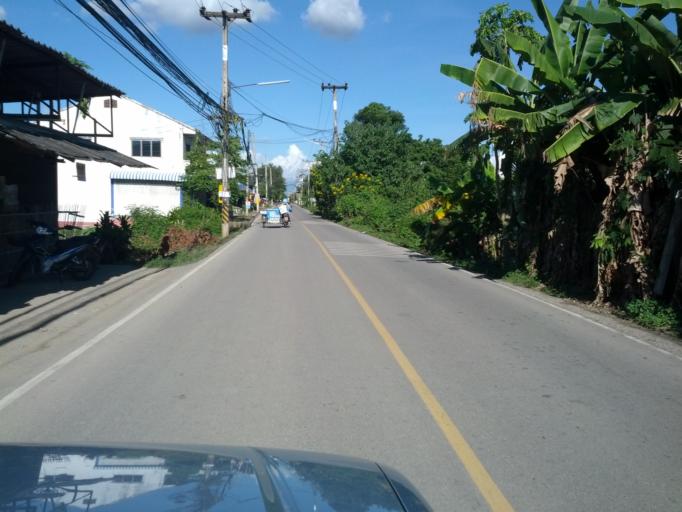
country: TH
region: Chiang Mai
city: Saraphi
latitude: 18.6866
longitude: 98.9961
